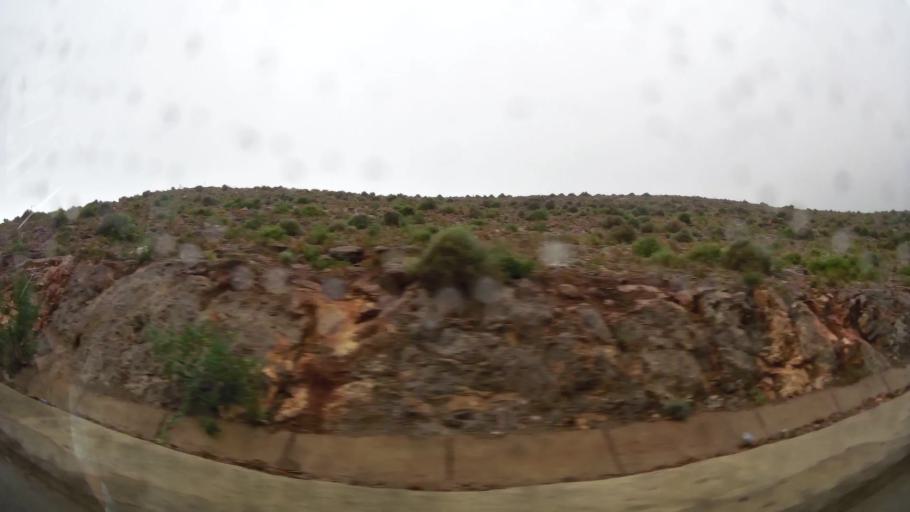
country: MA
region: Taza-Al Hoceima-Taounate
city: Al Hoceima
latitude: 35.2572
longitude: -3.9355
